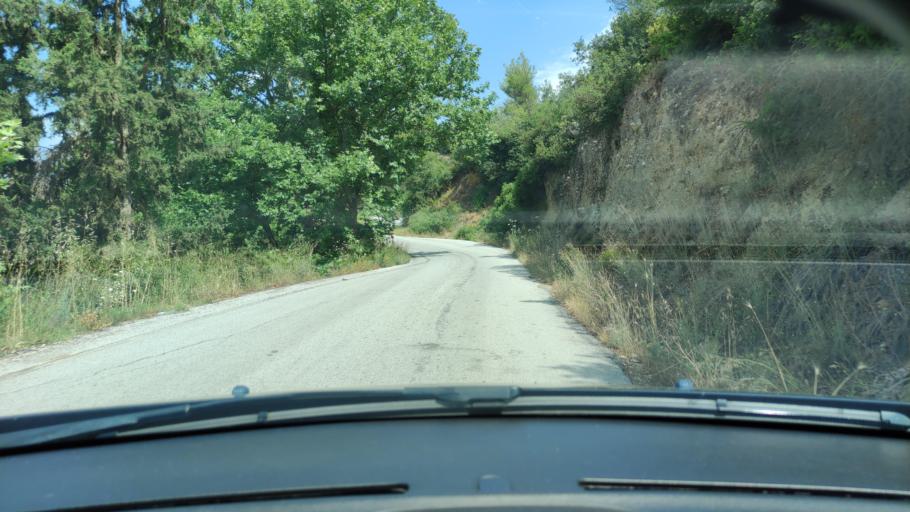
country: GR
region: Central Greece
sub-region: Nomos Evvoias
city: Afration
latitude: 38.5146
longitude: 23.7759
